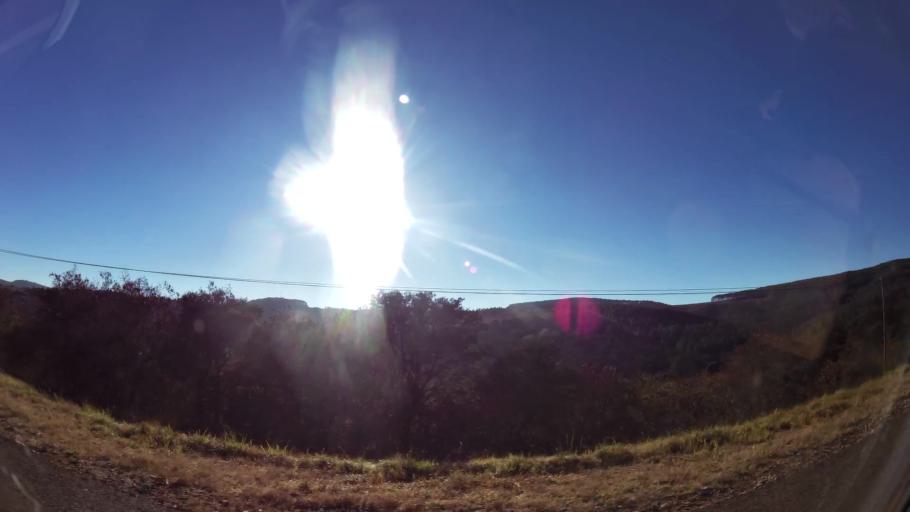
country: ZA
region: Limpopo
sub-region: Capricorn District Municipality
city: Mankoeng
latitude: -23.9261
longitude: 29.8938
